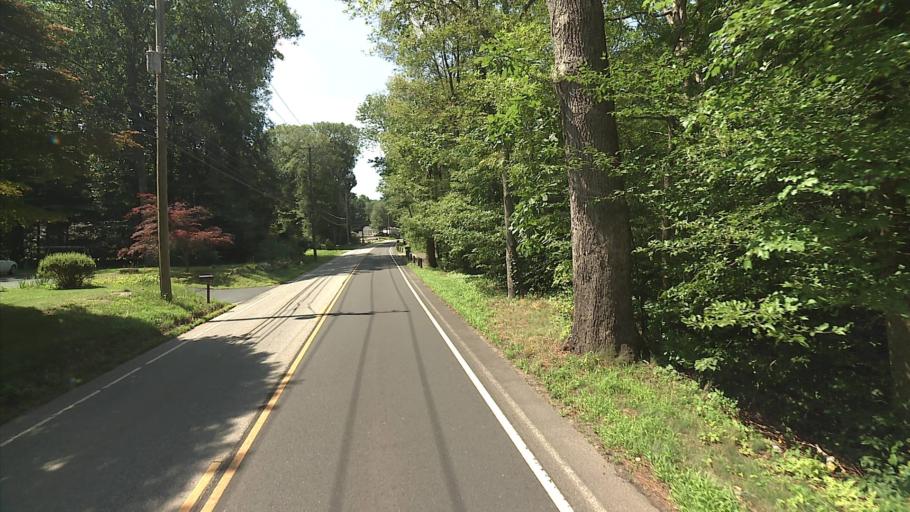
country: US
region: Connecticut
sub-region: Middlesex County
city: Westbrook Center
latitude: 41.3119
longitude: -72.4350
